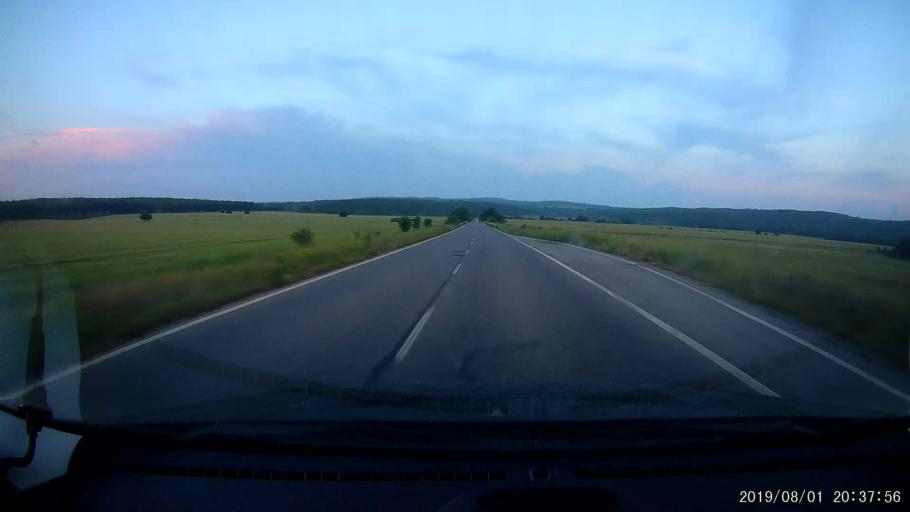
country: BG
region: Yambol
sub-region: Obshtina Elkhovo
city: Elkhovo
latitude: 42.0371
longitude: 26.5969
